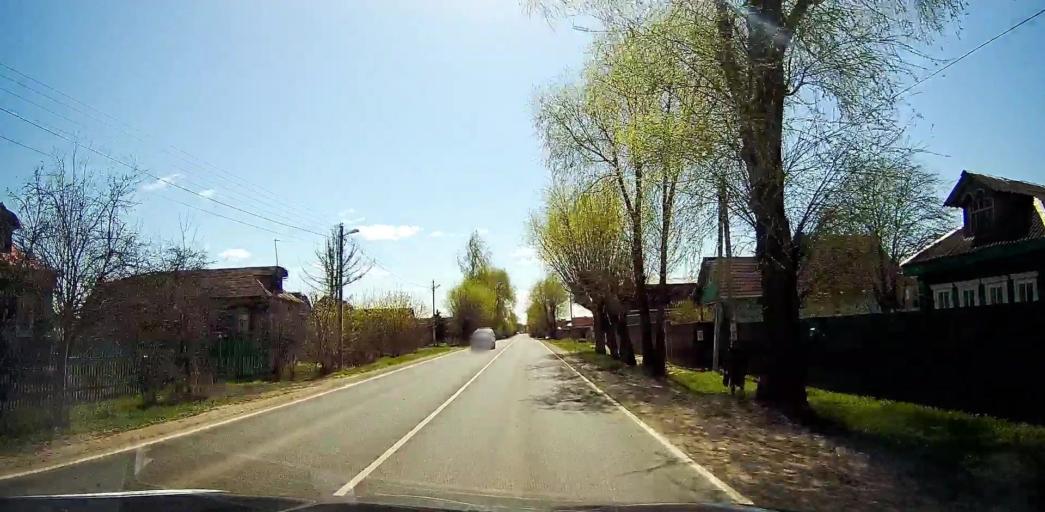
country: RU
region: Moskovskaya
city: Beloozerskiy
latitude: 55.5152
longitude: 38.4325
